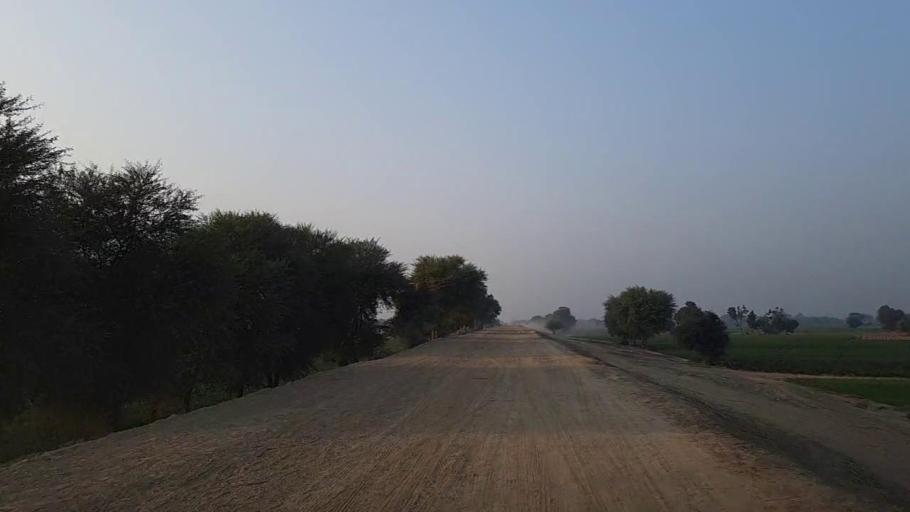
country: PK
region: Sindh
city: Sann
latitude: 26.1809
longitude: 68.0951
